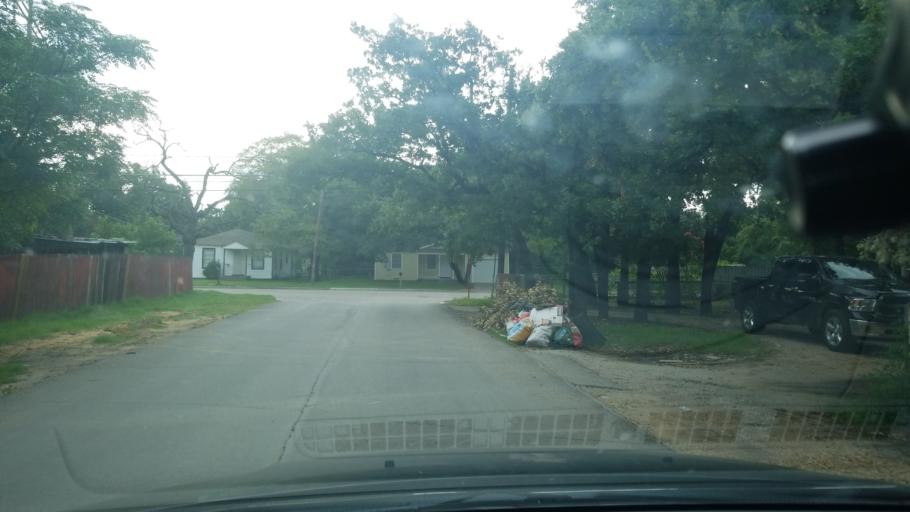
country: US
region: Texas
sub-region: Dallas County
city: Balch Springs
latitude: 32.7287
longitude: -96.6575
